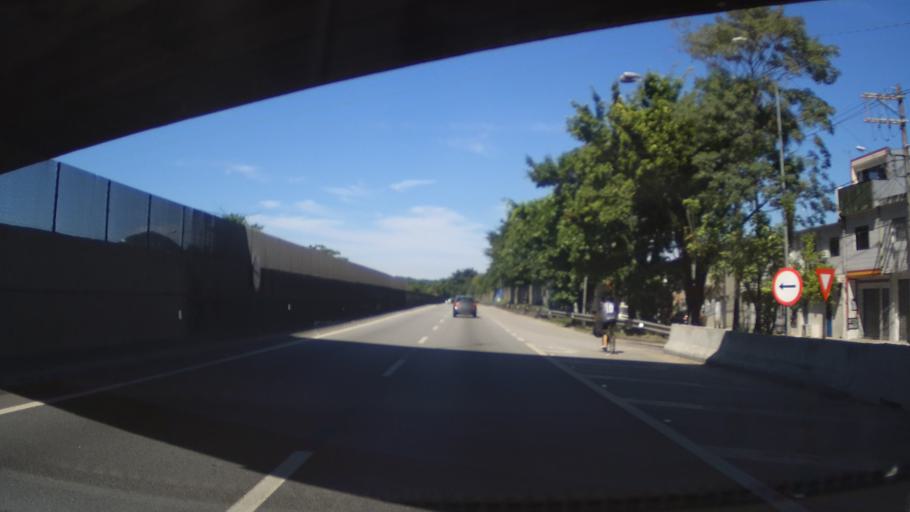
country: BR
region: Sao Paulo
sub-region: Sao Vicente
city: Sao Vicente
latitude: -23.9687
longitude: -46.4009
